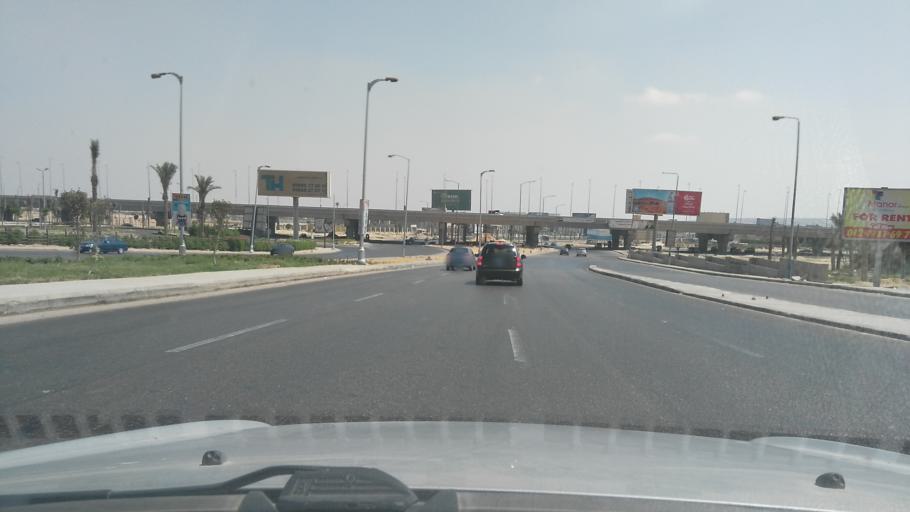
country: EG
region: Al Jizah
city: Awsim
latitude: 30.0071
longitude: 30.9795
